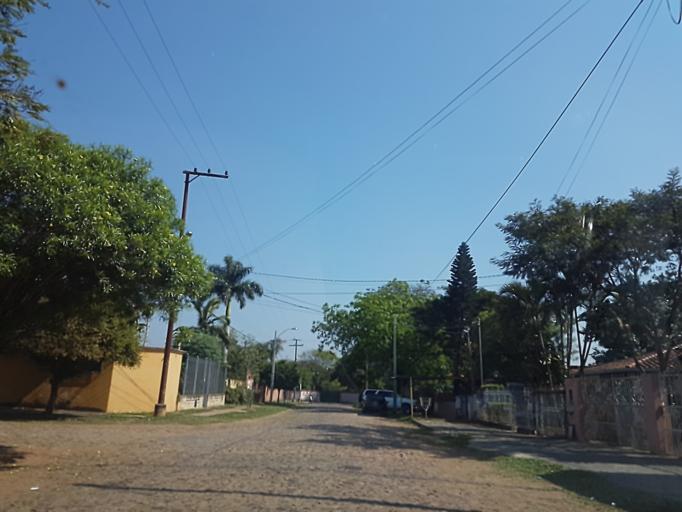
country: PY
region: Central
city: Colonia Mariano Roque Alonso
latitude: -25.2147
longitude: -57.5252
